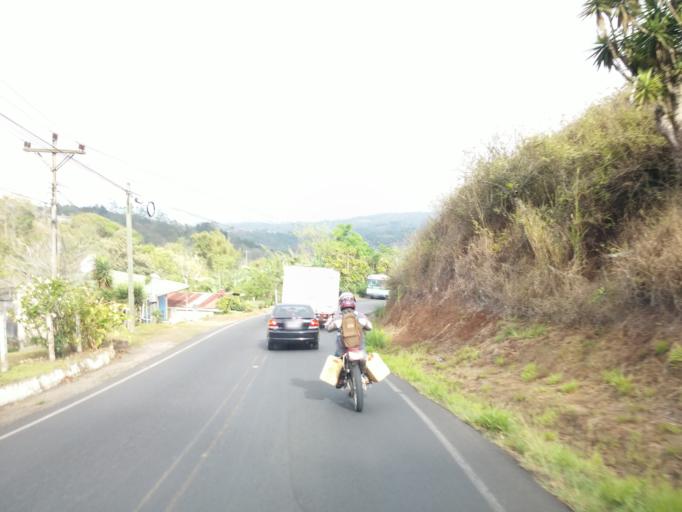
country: CR
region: Alajuela
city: San Ramon
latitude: 10.1166
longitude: -84.4700
